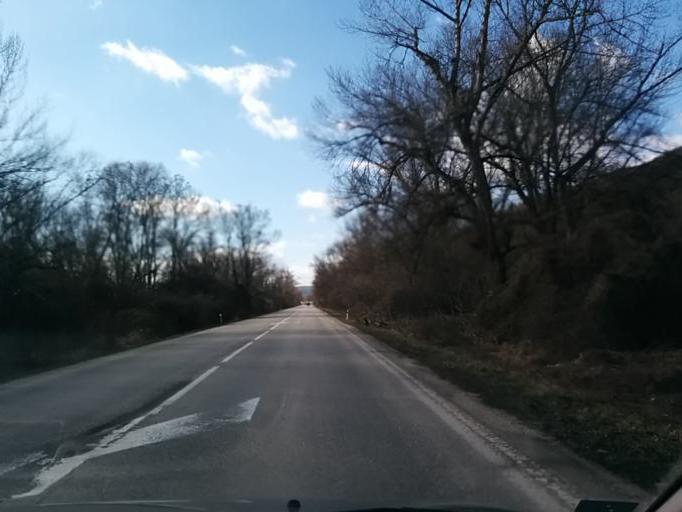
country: SK
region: Trenciansky
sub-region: Okres Nove Mesto nad Vahom
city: Nove Mesto nad Vahom
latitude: 48.7797
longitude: 17.8597
